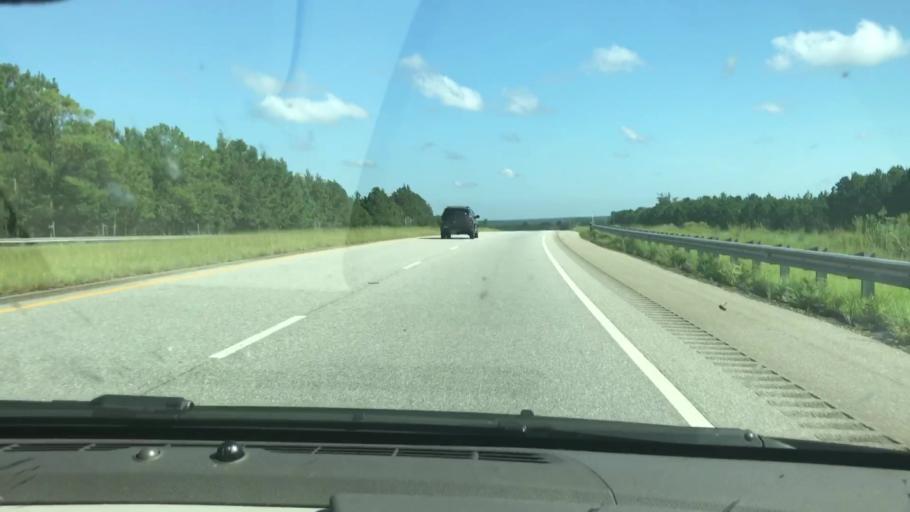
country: US
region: Alabama
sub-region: Barbour County
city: Eufaula
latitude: 32.1594
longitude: -85.1781
